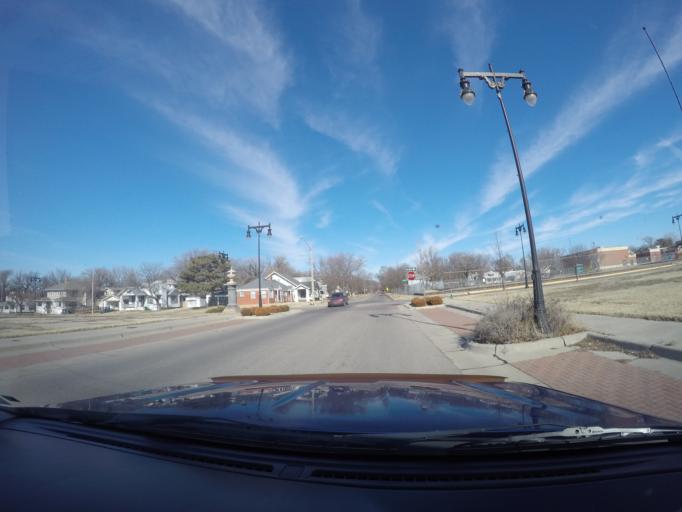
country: US
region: Kansas
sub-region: Sedgwick County
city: Wichita
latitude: 37.6879
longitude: -97.2966
